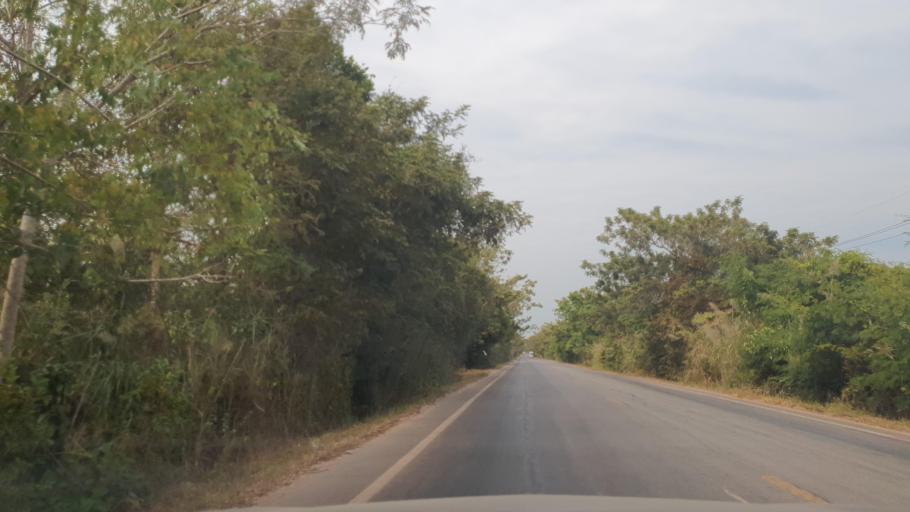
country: TH
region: Changwat Bueng Kan
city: Bung Khla
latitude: 18.2182
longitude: 104.0396
